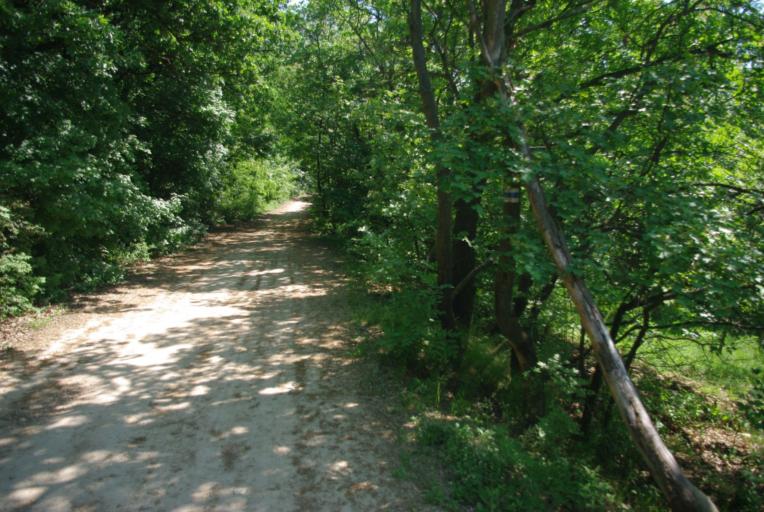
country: HU
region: Pest
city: Pilisborosjeno
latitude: 47.6168
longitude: 18.9777
